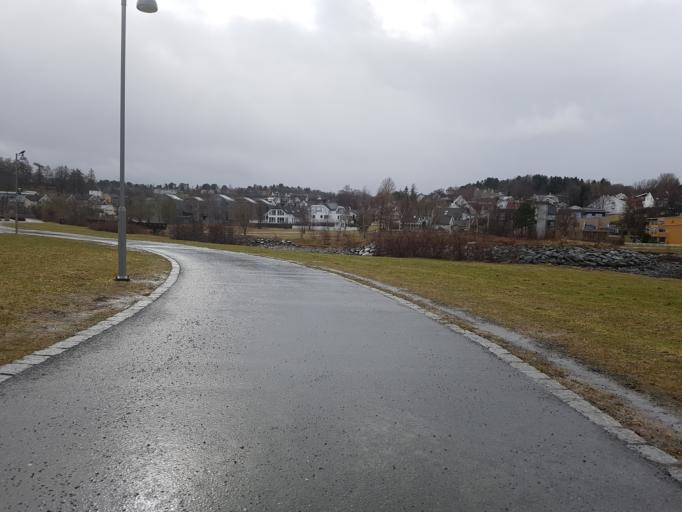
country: NO
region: Sor-Trondelag
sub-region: Trondheim
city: Trondheim
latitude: 63.4366
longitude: 10.5005
